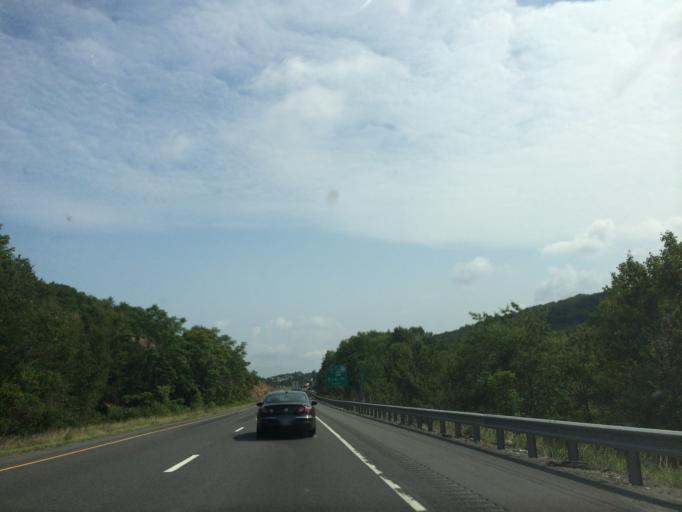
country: US
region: Pennsylvania
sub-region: Lackawanna County
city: Scranton
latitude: 41.3797
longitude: -75.6658
